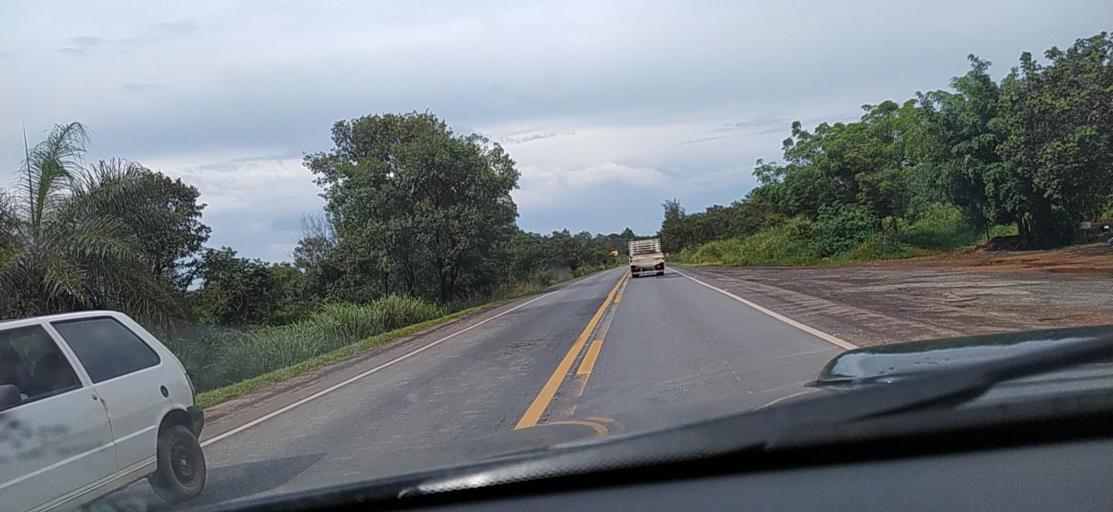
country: BR
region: Minas Gerais
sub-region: Montes Claros
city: Montes Claros
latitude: -16.8747
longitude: -43.8588
